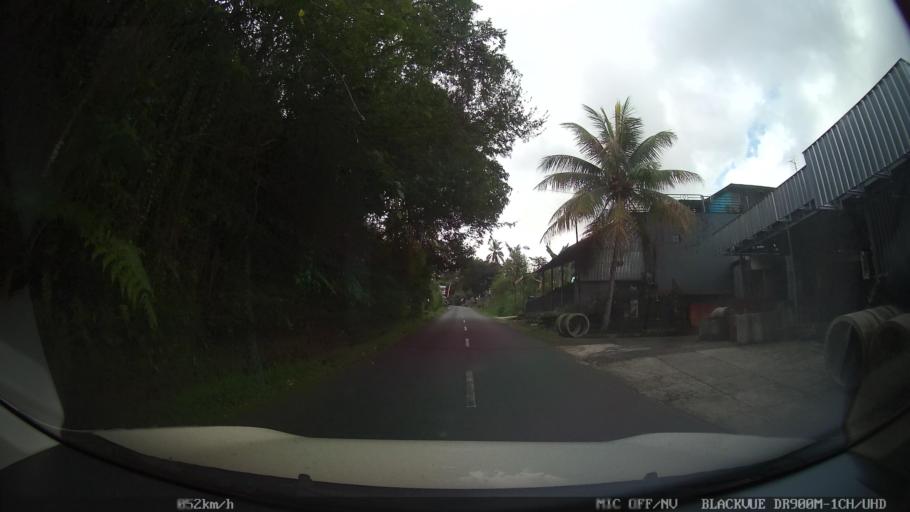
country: ID
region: Bali
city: Bangli
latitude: -8.4480
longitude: 115.3447
